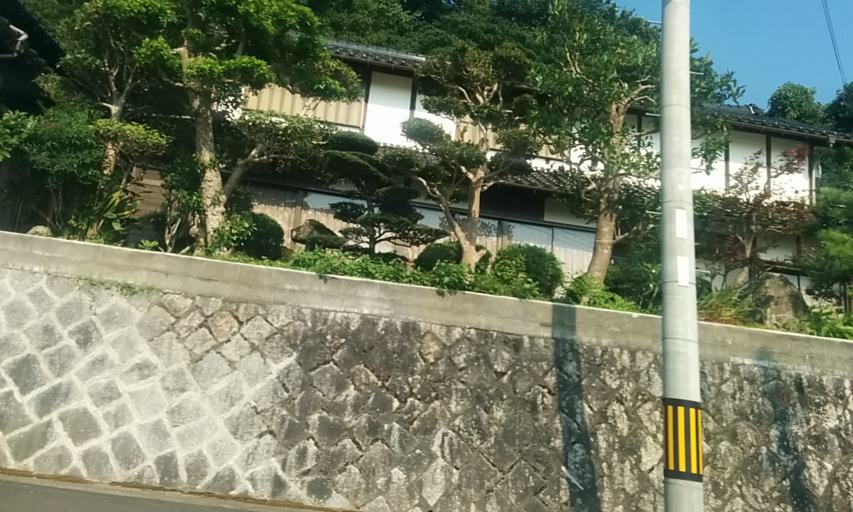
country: JP
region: Kyoto
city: Maizuru
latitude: 35.4594
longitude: 135.2870
